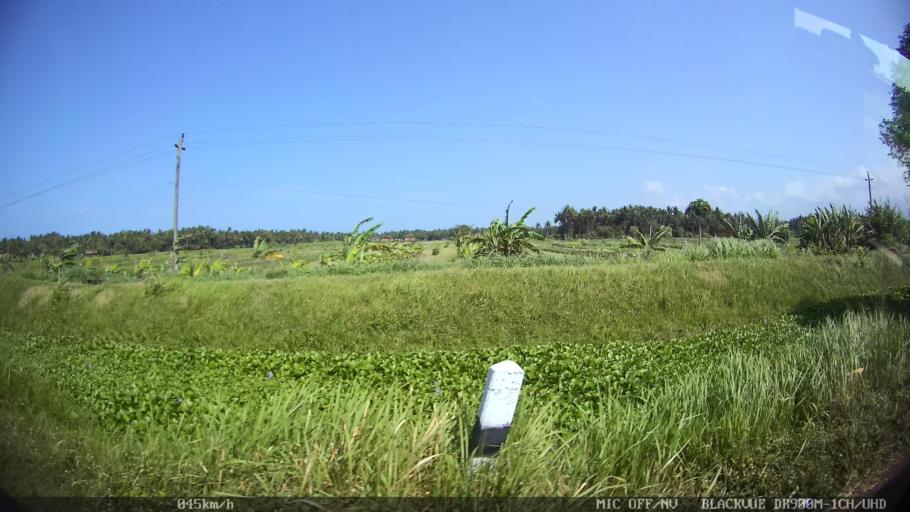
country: ID
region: Daerah Istimewa Yogyakarta
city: Srandakan
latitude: -7.9342
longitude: 110.1547
